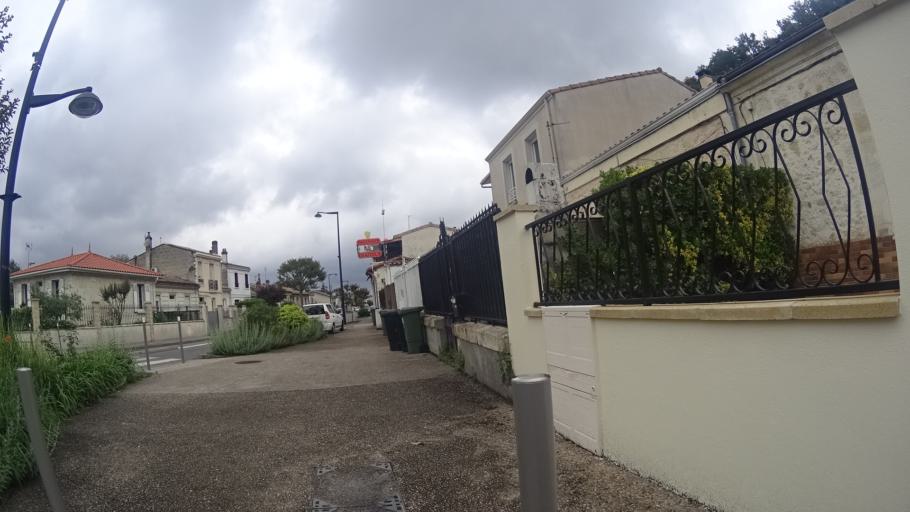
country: FR
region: Aquitaine
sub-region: Departement de la Gironde
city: Floirac
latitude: 44.8326
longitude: -0.5285
